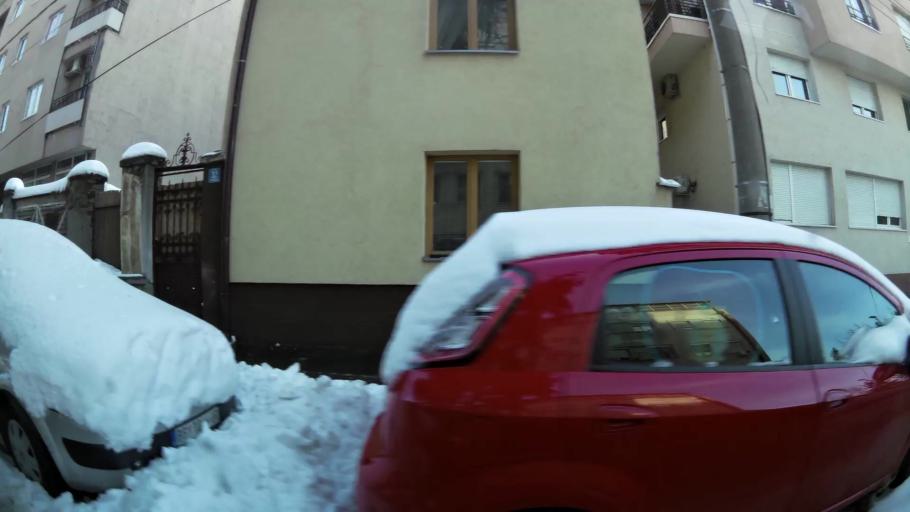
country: RS
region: Central Serbia
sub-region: Belgrade
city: Vracar
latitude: 44.7999
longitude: 20.4940
